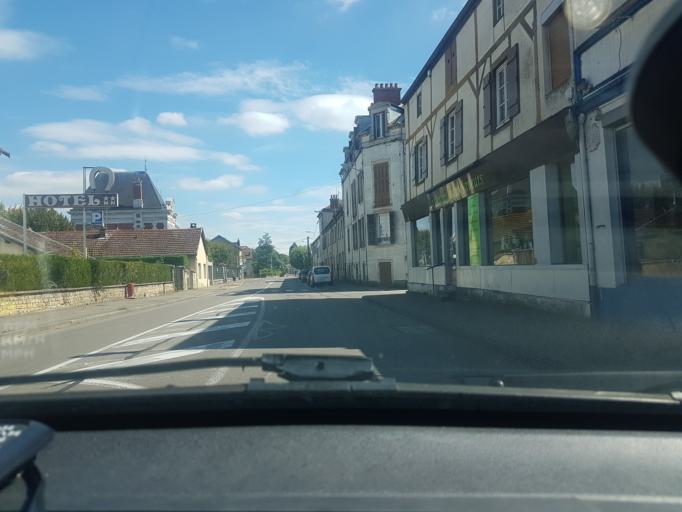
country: FR
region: Franche-Comte
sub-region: Departement de la Haute-Saone
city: Gray
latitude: 47.4484
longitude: 5.5931
